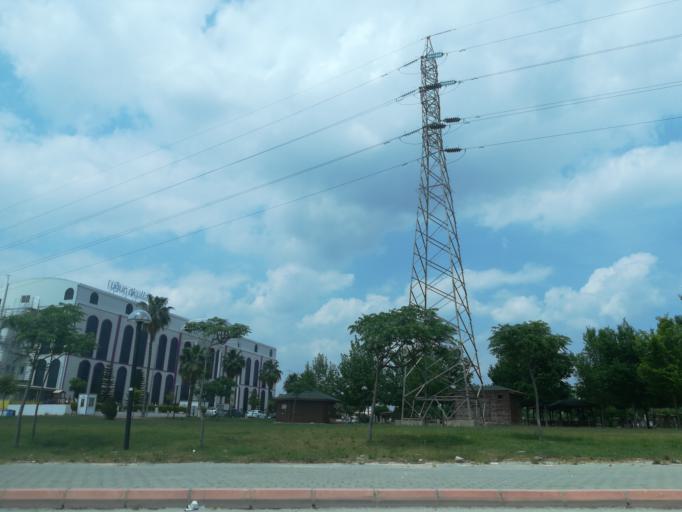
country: TR
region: Adana
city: Seyhan
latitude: 37.0052
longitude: 35.2510
